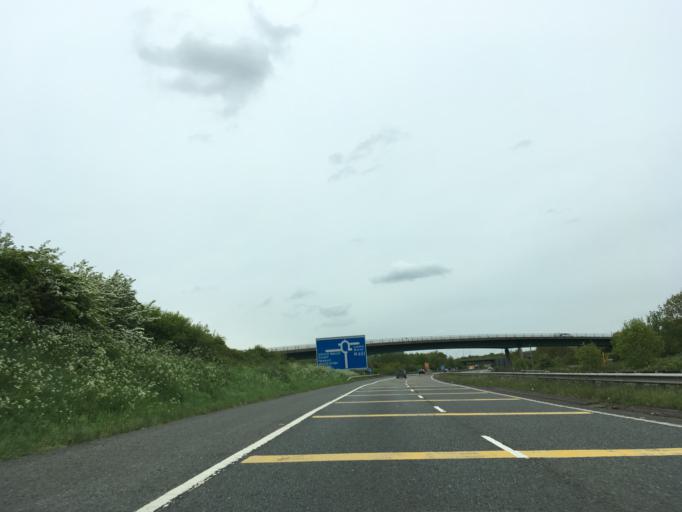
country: GB
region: England
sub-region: South Gloucestershire
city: Severn Beach
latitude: 51.5647
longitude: -2.6582
